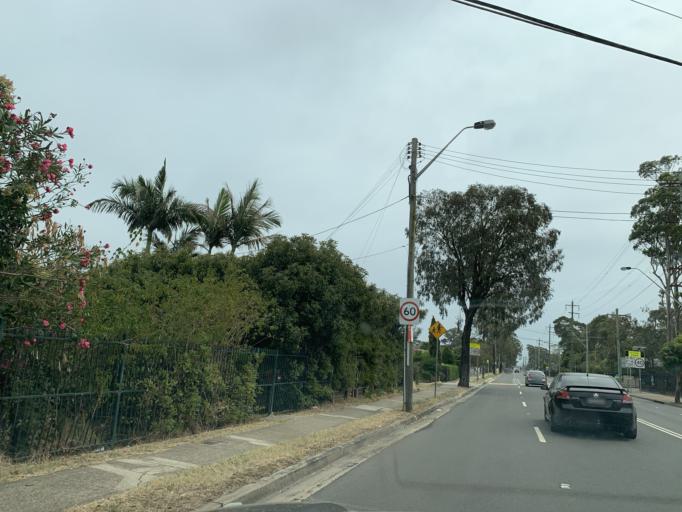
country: AU
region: New South Wales
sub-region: Blacktown
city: Blacktown
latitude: -33.7719
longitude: 150.8919
